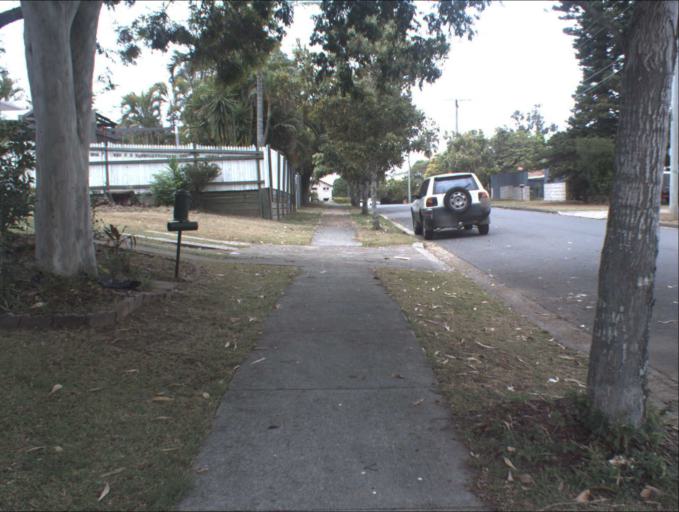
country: AU
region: Queensland
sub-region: Logan
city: Slacks Creek
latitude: -27.6429
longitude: 153.1417
